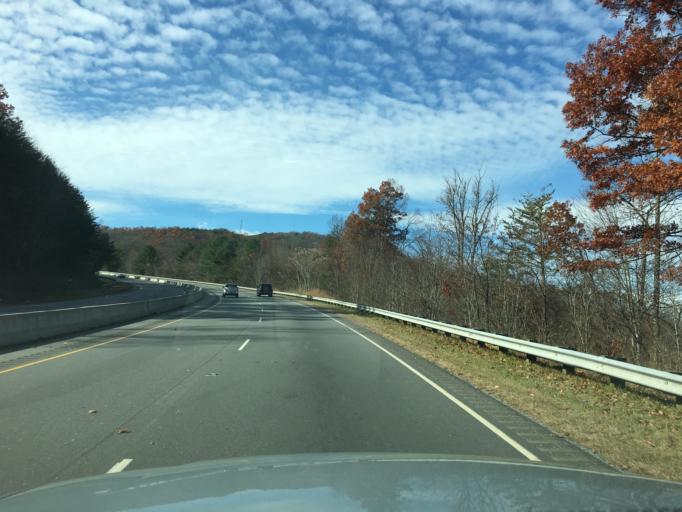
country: US
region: North Carolina
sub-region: McDowell County
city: Marion
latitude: 35.6694
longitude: -81.9918
